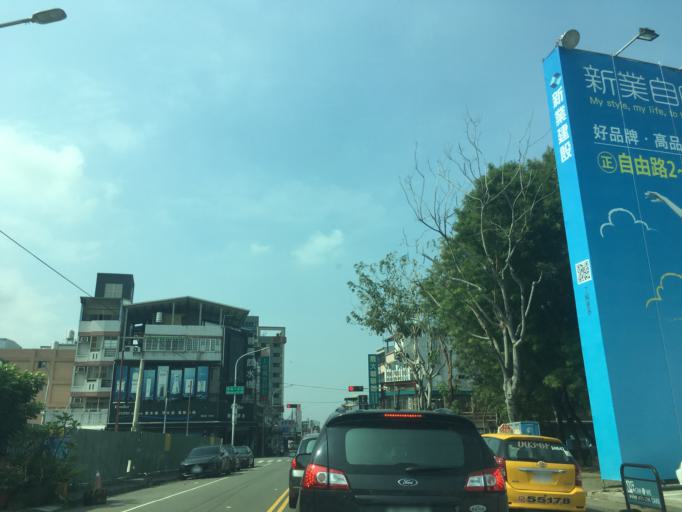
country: TW
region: Taiwan
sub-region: Taichung City
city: Taichung
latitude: 24.1467
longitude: 120.7098
